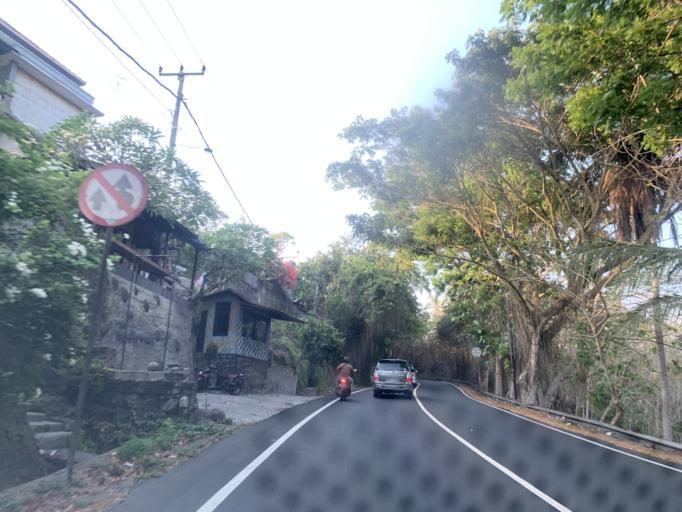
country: ID
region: Bali
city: Banjar Delodrurung
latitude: -8.4977
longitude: 114.9668
